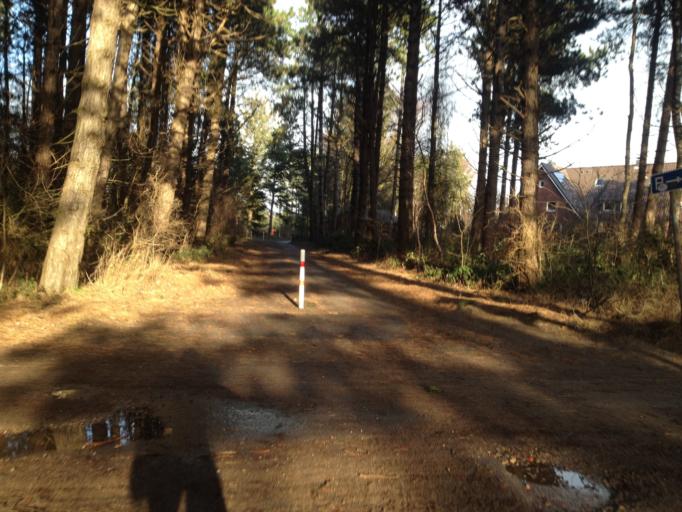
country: DE
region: Schleswig-Holstein
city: Nebel
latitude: 54.6406
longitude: 8.3482
